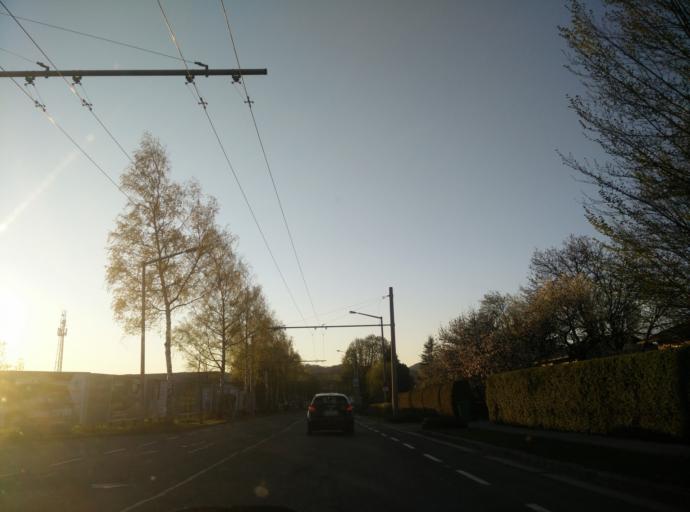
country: AT
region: Salzburg
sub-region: Salzburg Stadt
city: Salzburg
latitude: 47.8213
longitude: 13.0672
